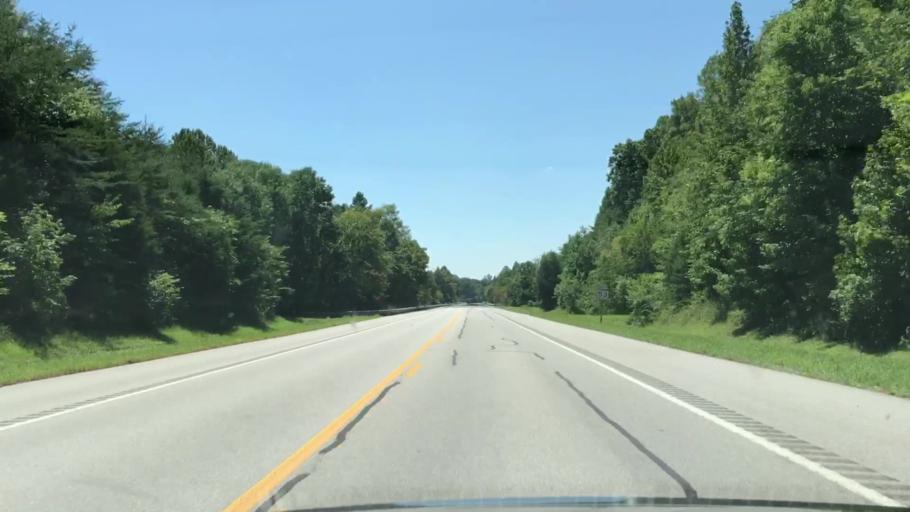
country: US
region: Tennessee
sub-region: Clay County
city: Celina
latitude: 36.5908
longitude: -85.4423
